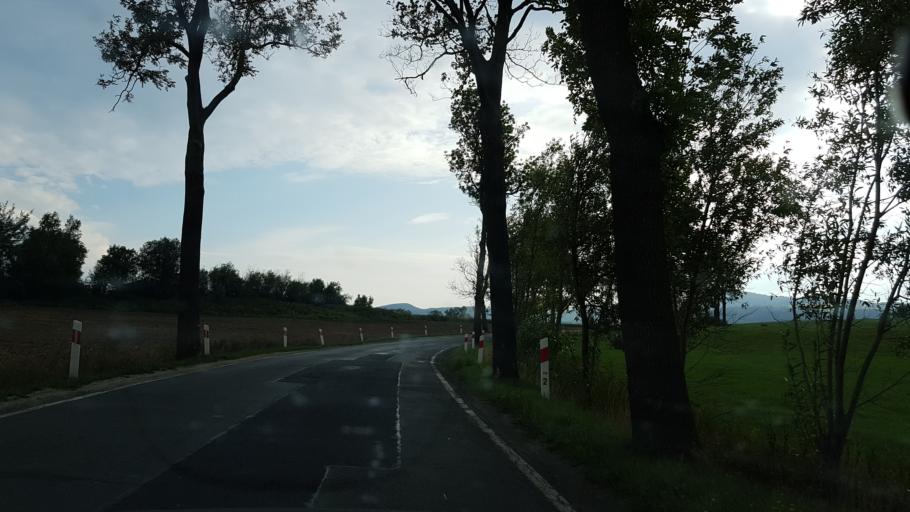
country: PL
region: Lower Silesian Voivodeship
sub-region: Powiat kamiennogorski
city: Marciszow
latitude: 50.8718
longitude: 16.0014
